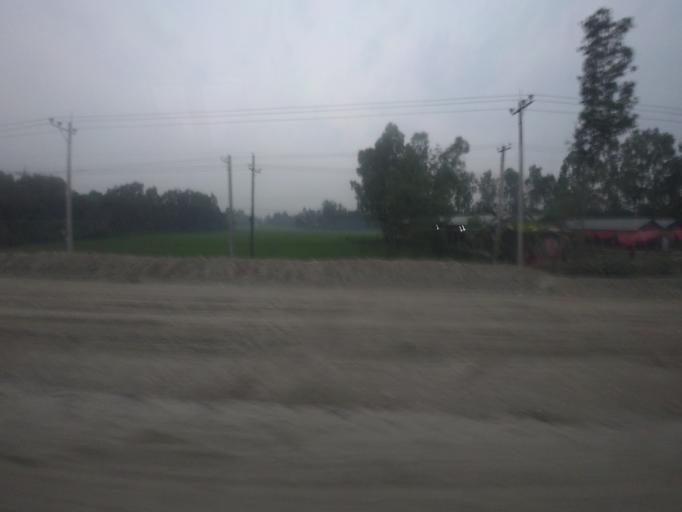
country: BD
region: Dhaka
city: Tangail
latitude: 24.3237
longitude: 89.9243
